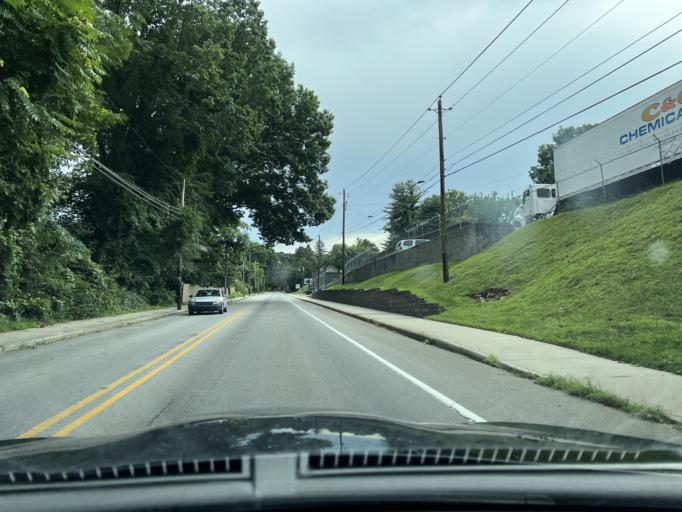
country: US
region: North Carolina
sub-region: Buncombe County
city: Asheville
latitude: 35.5818
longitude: -82.5724
